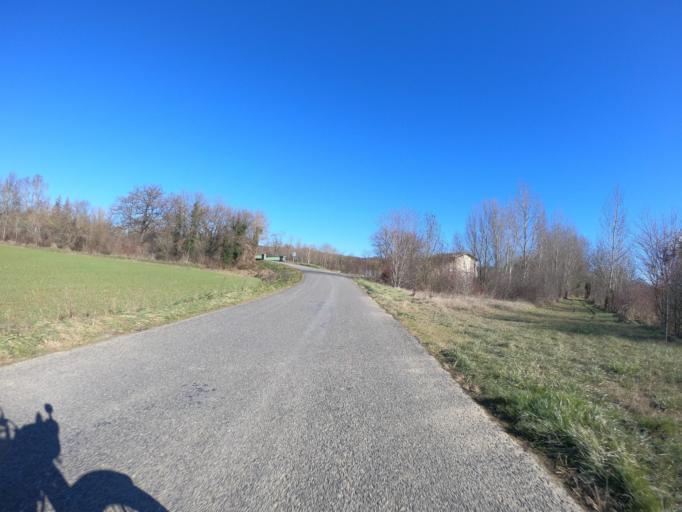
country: FR
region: Midi-Pyrenees
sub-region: Departement de l'Ariege
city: La Tour-du-Crieu
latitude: 43.0972
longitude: 1.7442
